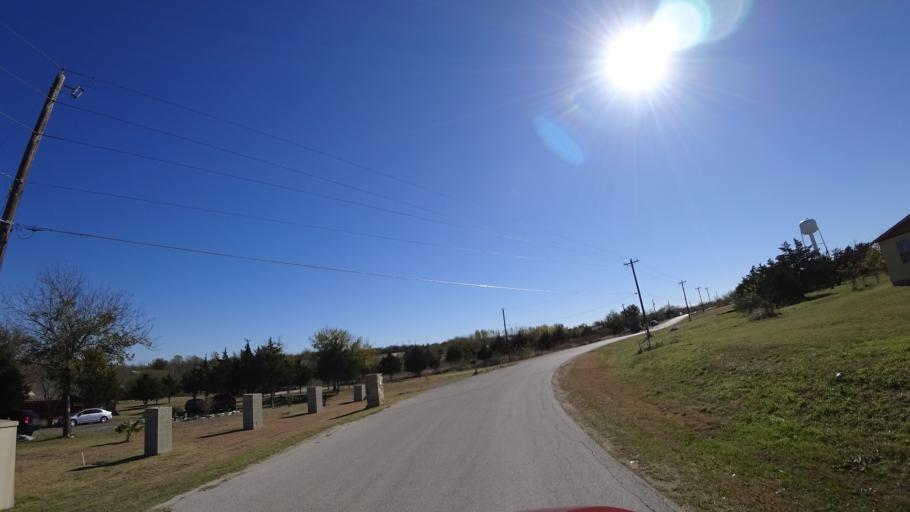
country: US
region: Texas
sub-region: Travis County
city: Garfield
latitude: 30.1023
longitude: -97.5989
